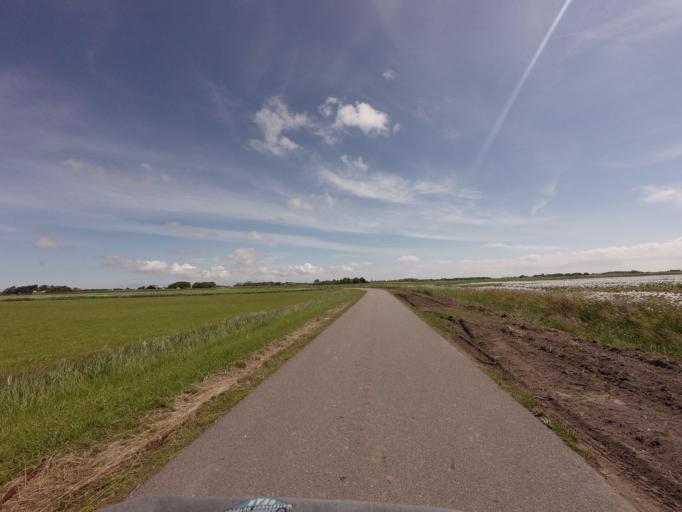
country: NL
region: North Holland
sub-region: Gemeente Texel
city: Den Burg
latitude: 53.0435
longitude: 4.7700
